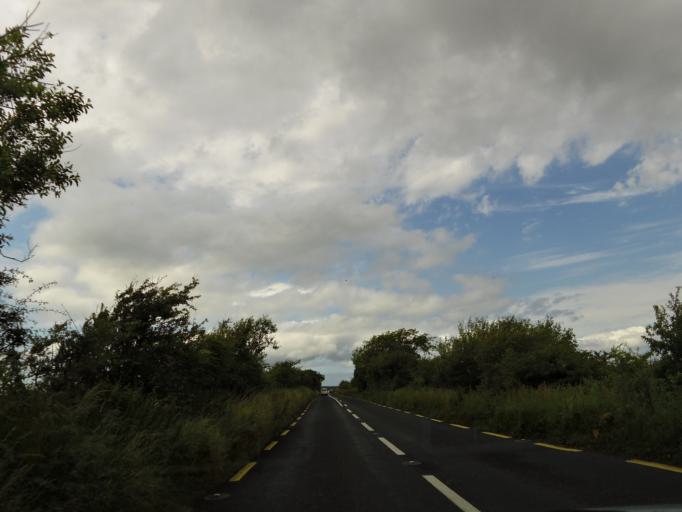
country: IE
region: Munster
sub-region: An Clar
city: Kilrush
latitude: 52.6571
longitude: -9.5258
